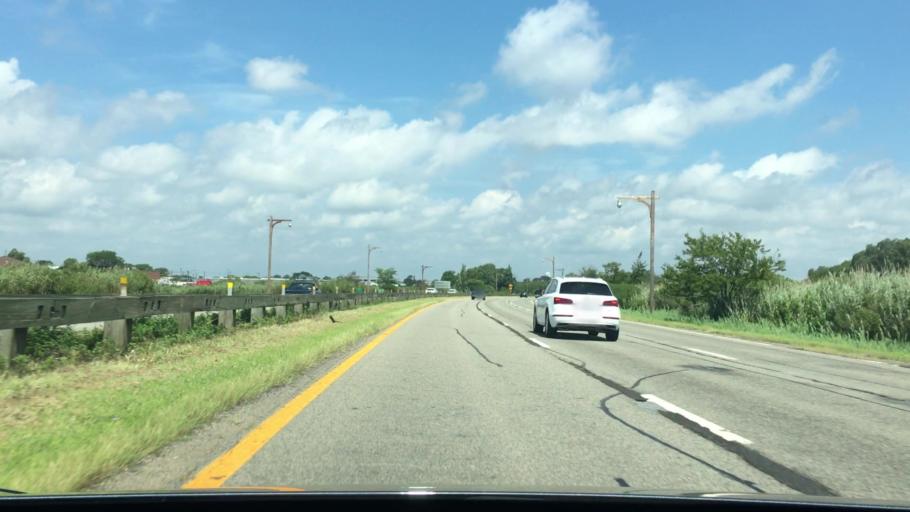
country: US
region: New York
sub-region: Nassau County
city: Freeport
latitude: 40.6436
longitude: -73.5647
